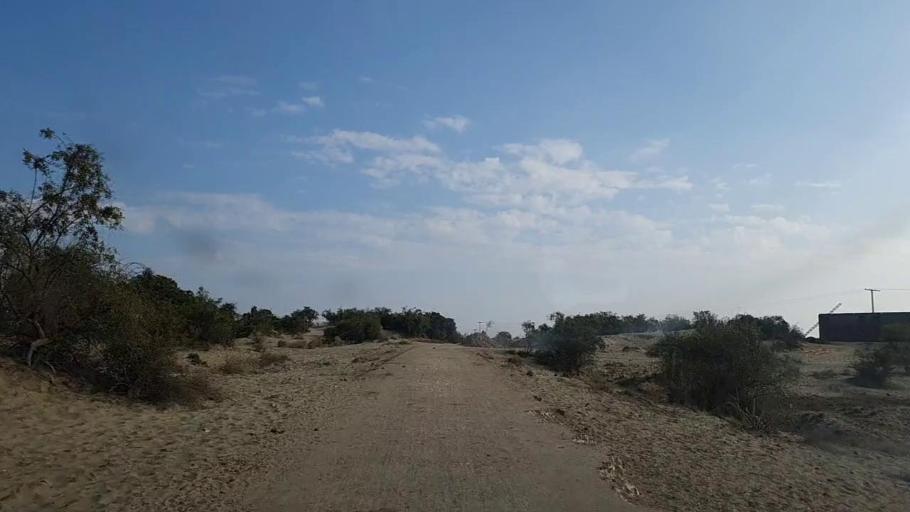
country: PK
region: Sindh
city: Sanghar
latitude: 26.2034
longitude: 69.0261
